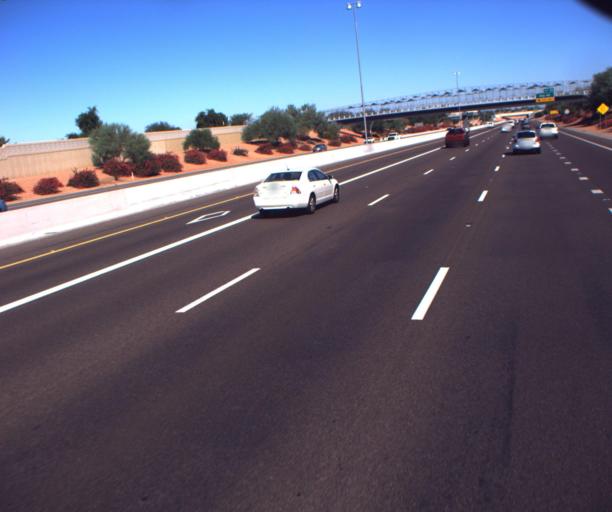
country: US
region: Arizona
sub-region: Maricopa County
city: Chandler
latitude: 33.3111
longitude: -111.8942
